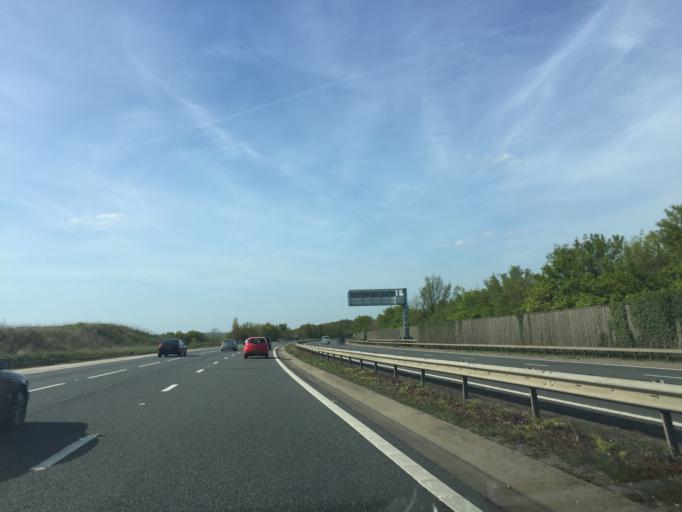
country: GB
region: England
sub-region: Kent
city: Swanley
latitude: 51.3938
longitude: 0.1610
